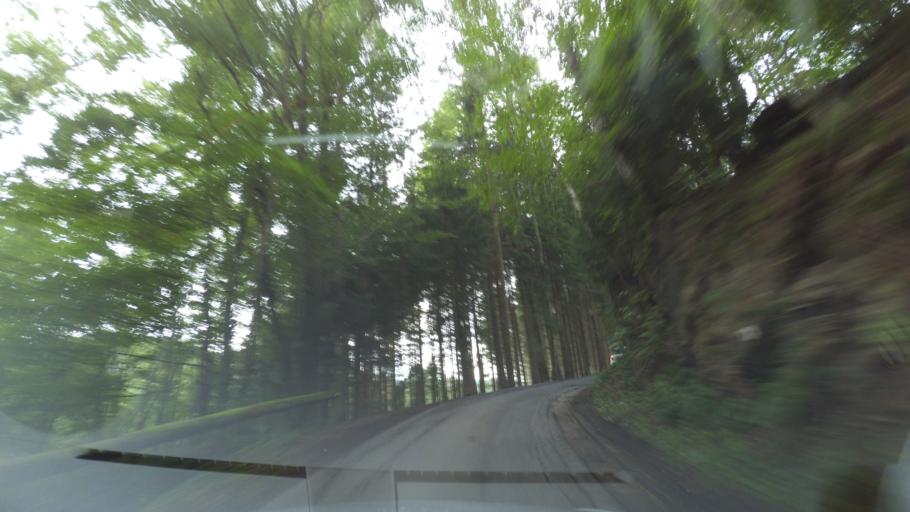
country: DE
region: Bavaria
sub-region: Upper Palatinate
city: Lohberg
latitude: 49.1585
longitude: 13.1124
